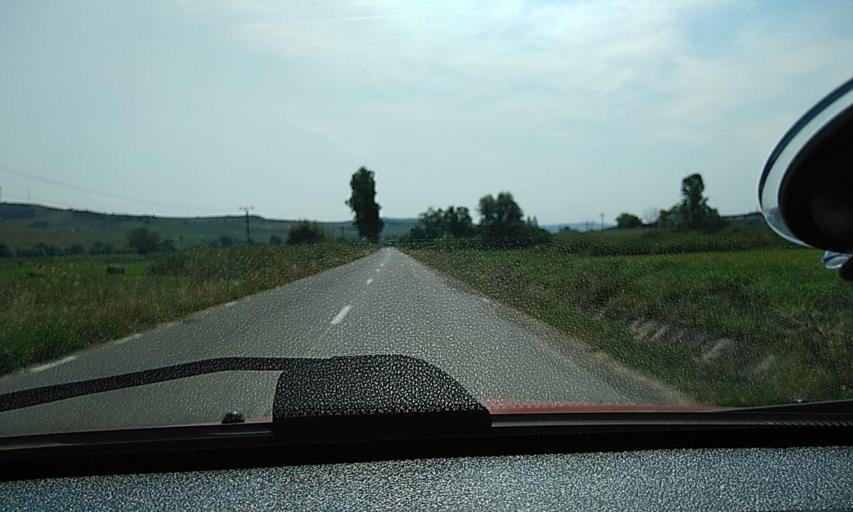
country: RO
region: Brasov
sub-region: Oras Rupea
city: Fiser
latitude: 46.0551
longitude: 25.1047
